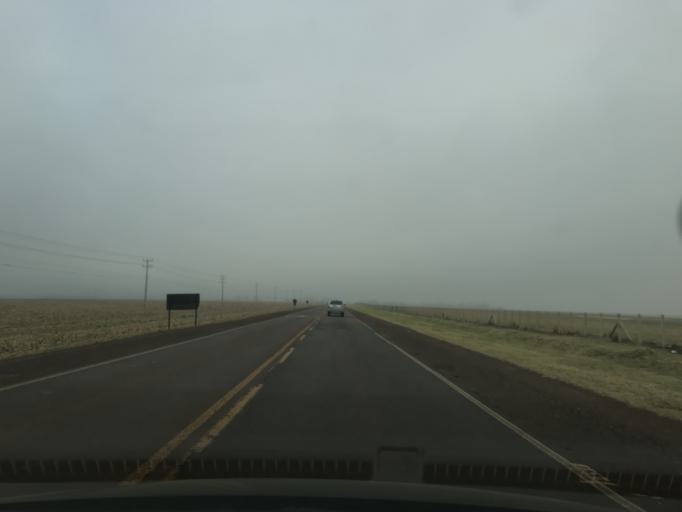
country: BR
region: Parana
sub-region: Toledo
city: Toledo
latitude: -24.6880
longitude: -53.6959
